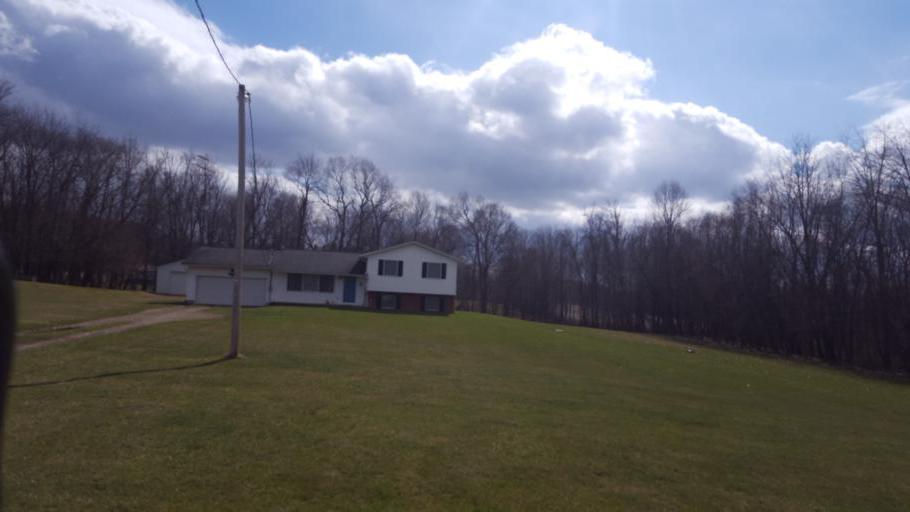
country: US
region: Ohio
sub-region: Richland County
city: Lincoln Heights
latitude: 40.6899
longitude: -82.4289
